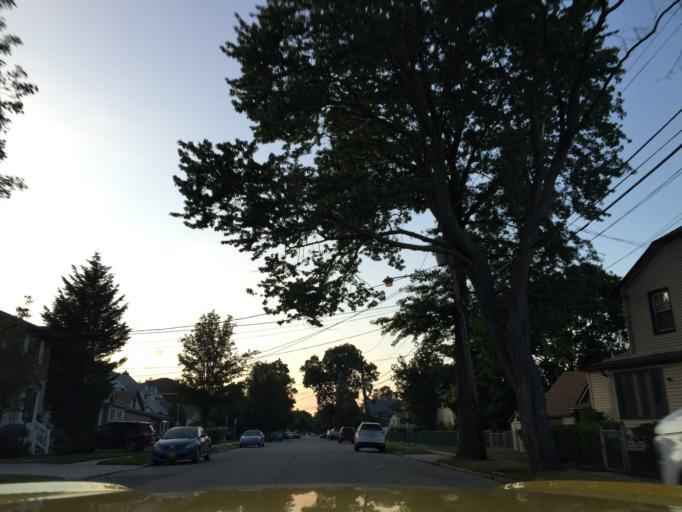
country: US
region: New York
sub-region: Nassau County
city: North New Hyde Park
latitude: 40.7356
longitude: -73.6998
